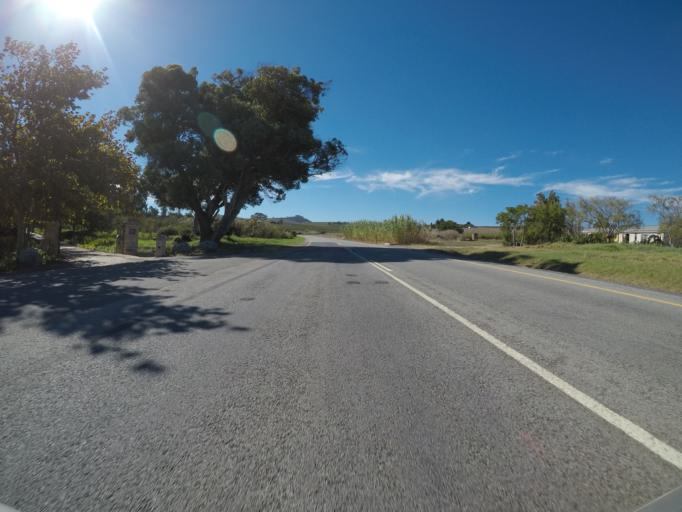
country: ZA
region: Western Cape
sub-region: Cape Winelands District Municipality
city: Stellenbosch
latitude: -33.9788
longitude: 18.7535
